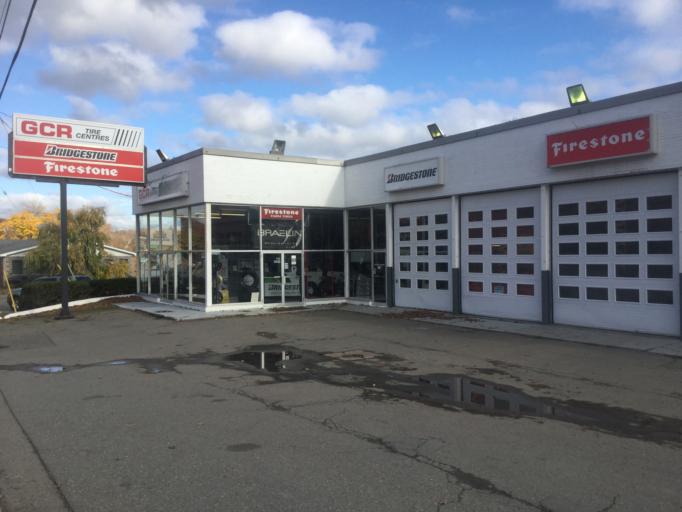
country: CA
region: Nova Scotia
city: New Glasgow
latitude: 45.5886
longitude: -62.6508
